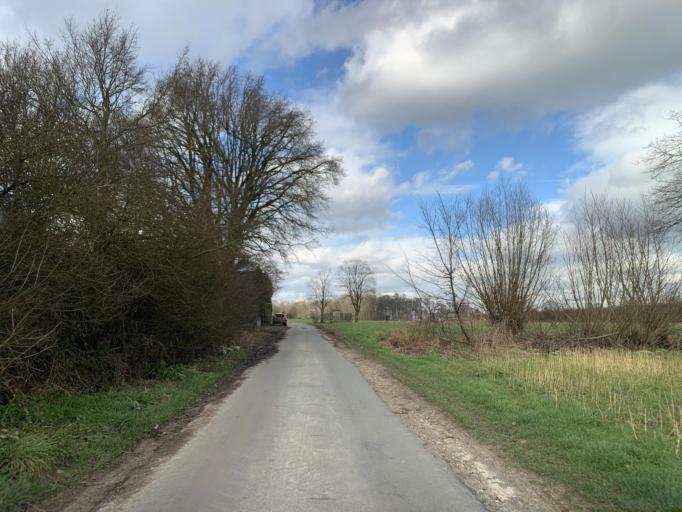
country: DE
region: North Rhine-Westphalia
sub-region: Regierungsbezirk Munster
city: Horstmar
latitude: 52.0858
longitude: 7.3172
